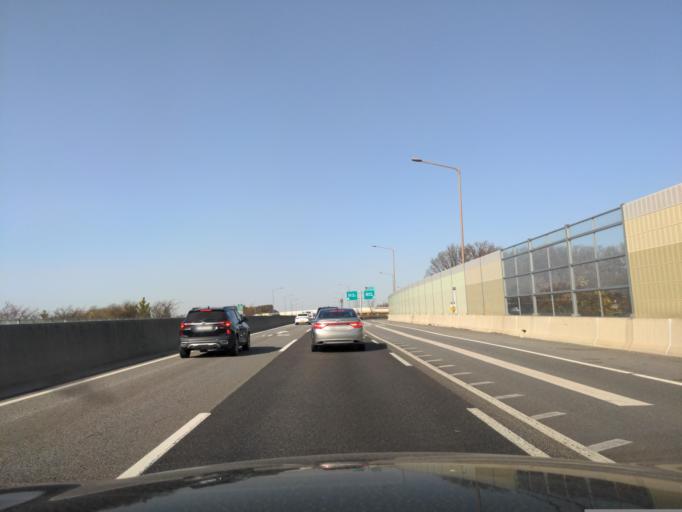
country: KR
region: Gyeonggi-do
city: Hwaseong-si
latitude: 37.1837
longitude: 126.7784
